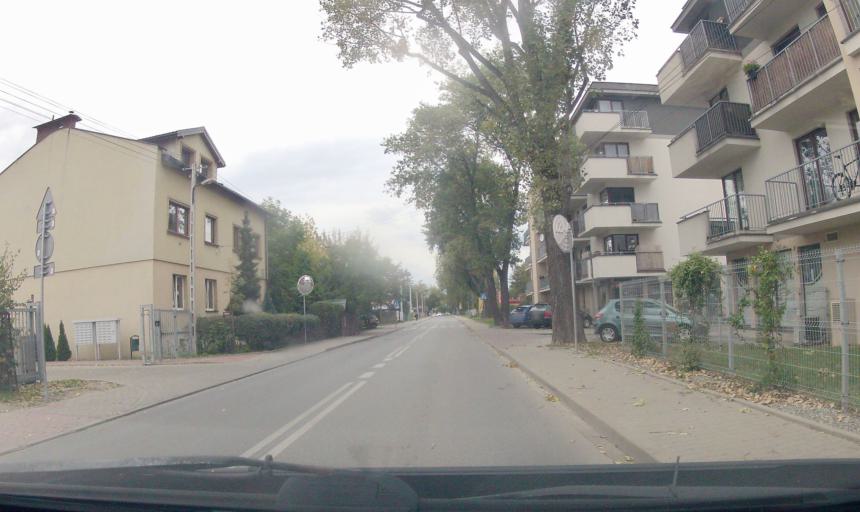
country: PL
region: Lesser Poland Voivodeship
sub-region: Krakow
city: Krakow
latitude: 50.0436
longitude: 19.9880
